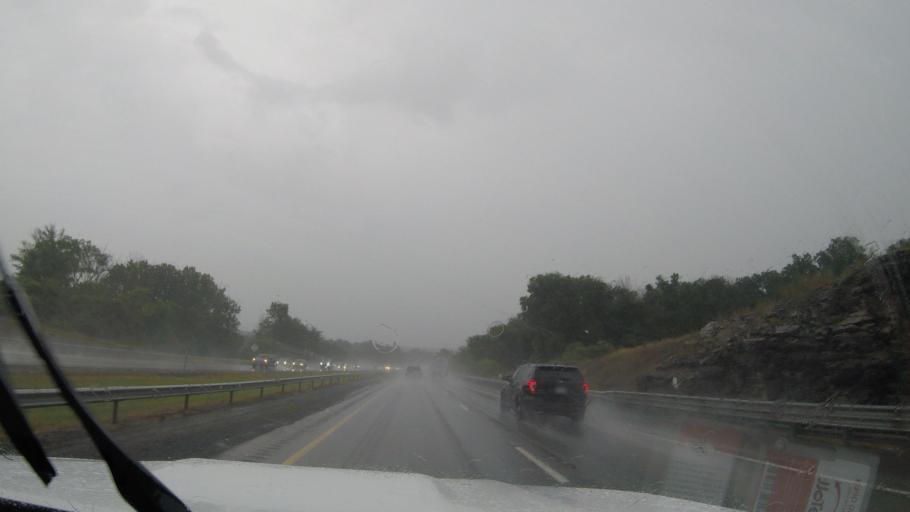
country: US
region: New York
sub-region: Ontario County
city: Phelps
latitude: 42.9690
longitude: -77.0687
